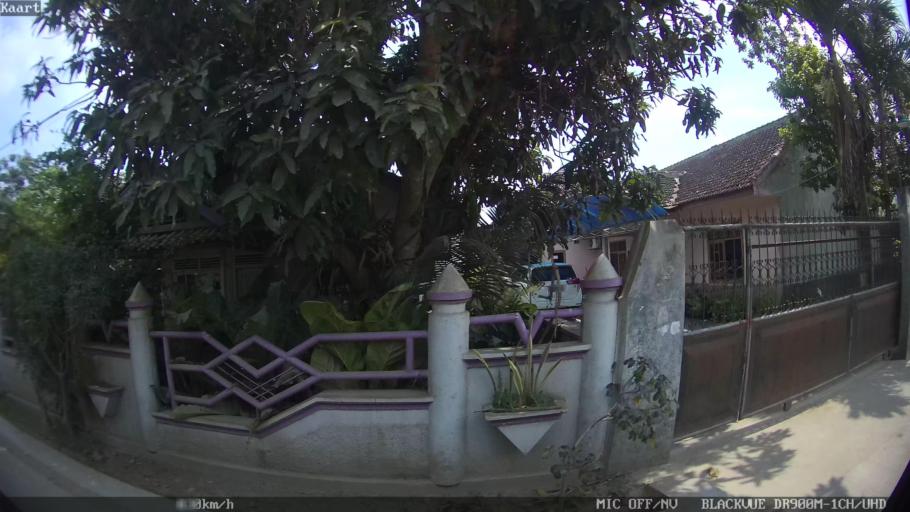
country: ID
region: Lampung
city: Pringsewu
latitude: -5.3622
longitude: 104.9805
